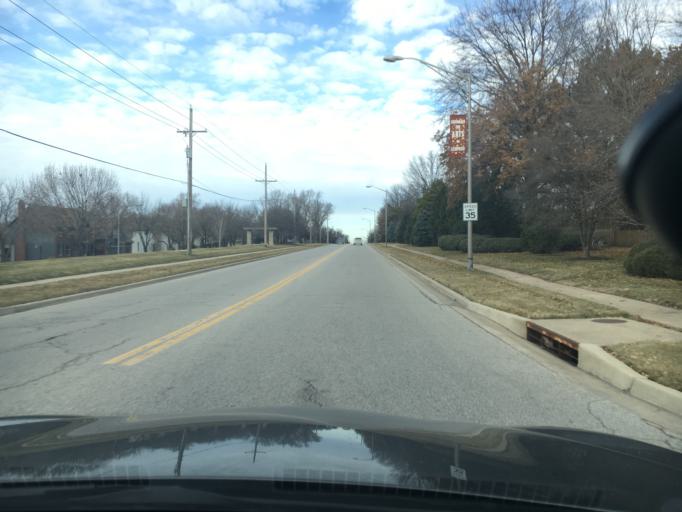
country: US
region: Kansas
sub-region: Johnson County
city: Leawood
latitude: 38.8940
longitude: -94.6305
